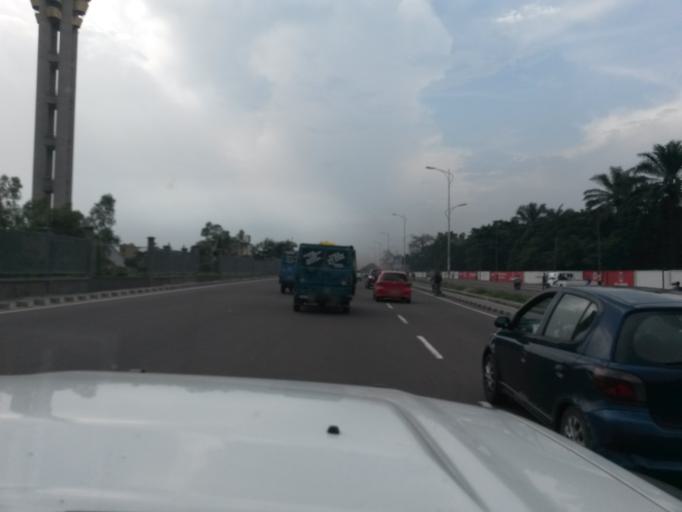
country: CD
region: Kinshasa
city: Masina
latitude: -4.3758
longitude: 15.3474
